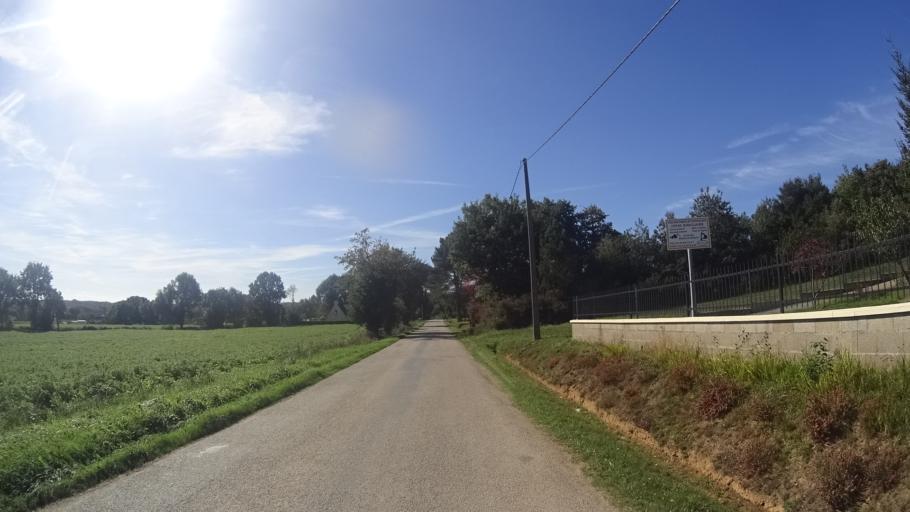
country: FR
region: Brittany
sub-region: Departement du Morbihan
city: Saint-Vincent-sur-Oust
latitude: 47.7349
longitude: -2.1569
